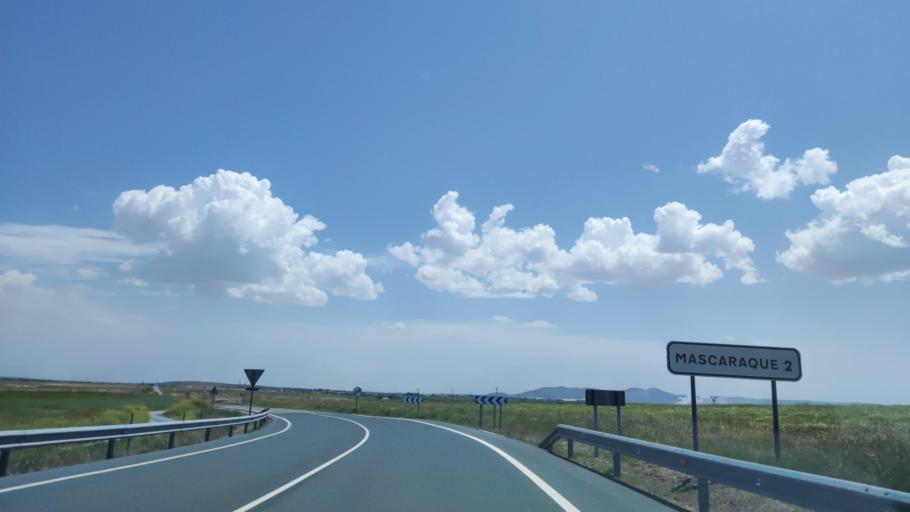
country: ES
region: Castille-La Mancha
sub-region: Province of Toledo
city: Mascaraque
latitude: 39.7123
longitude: -3.8378
